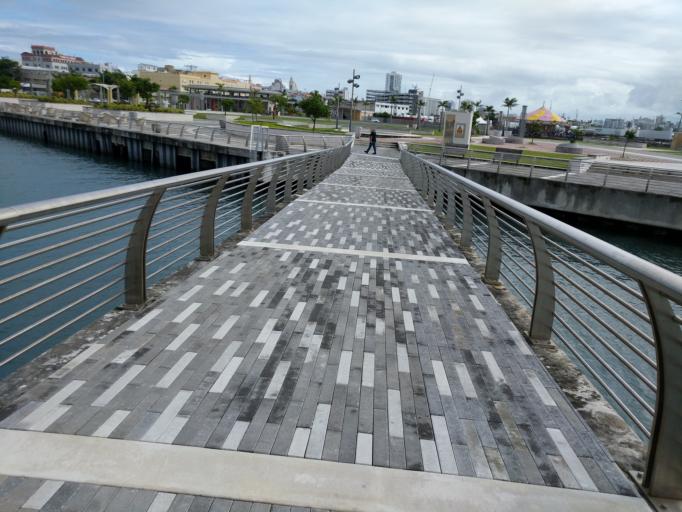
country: PR
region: San Juan
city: San Juan
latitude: 18.4636
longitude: -66.1064
